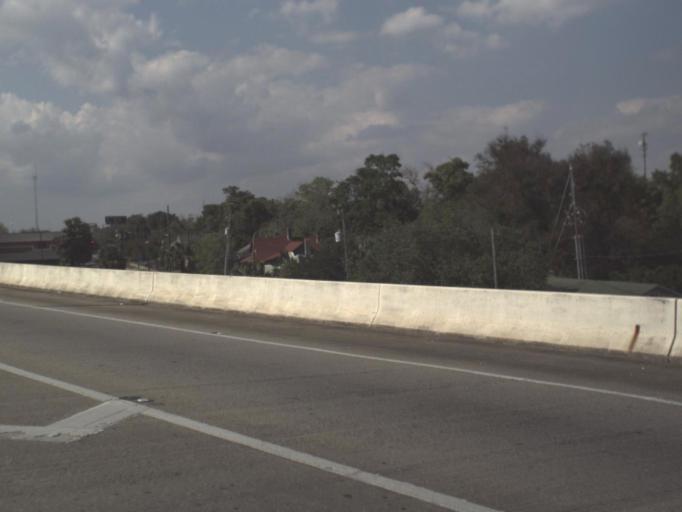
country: US
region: Florida
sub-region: Escambia County
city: Pensacola
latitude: 30.4185
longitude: -87.2128
